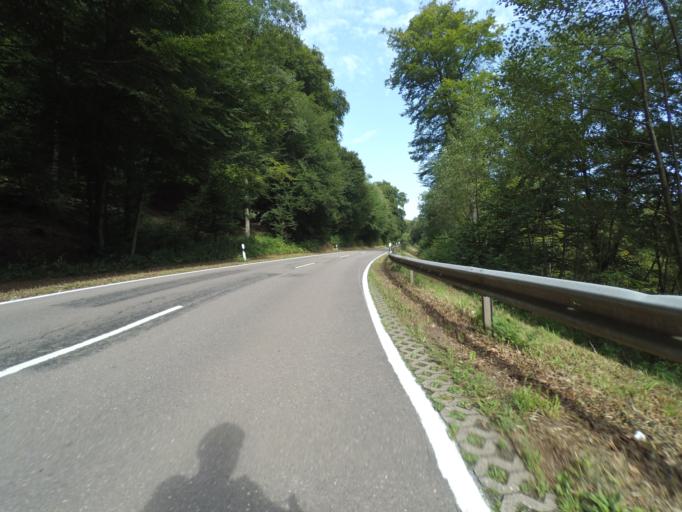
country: DE
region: Rheinland-Pfalz
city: Mannebach
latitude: 49.6298
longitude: 6.5274
